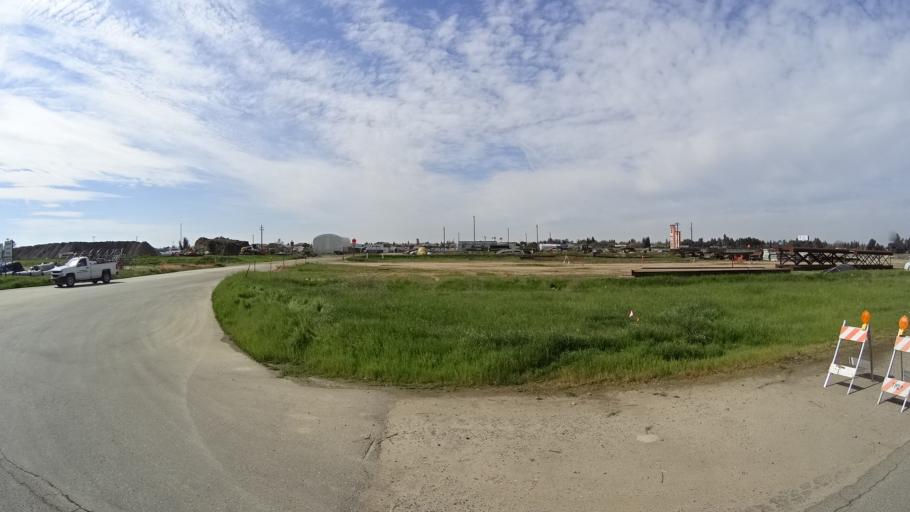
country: US
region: California
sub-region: Fresno County
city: Biola
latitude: 36.8297
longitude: -119.9089
